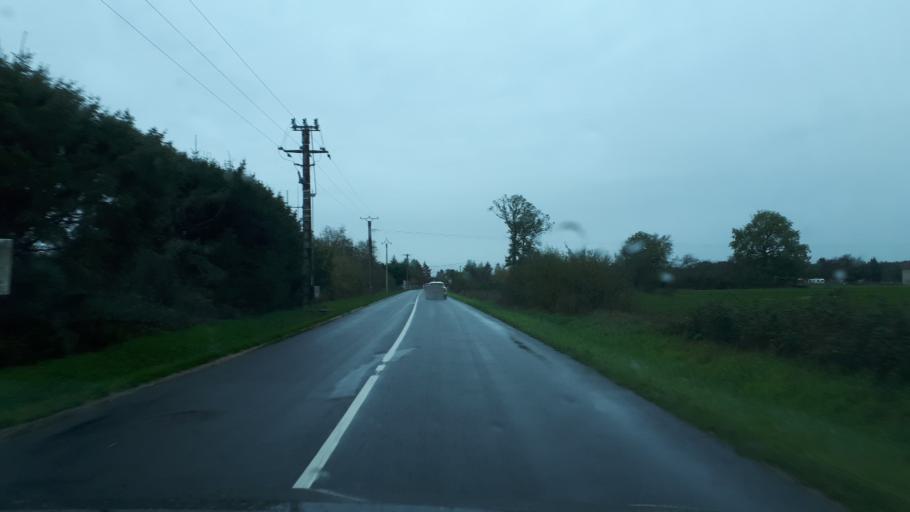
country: FR
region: Centre
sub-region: Departement du Loir-et-Cher
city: Gievres
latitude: 47.2839
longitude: 1.6681
